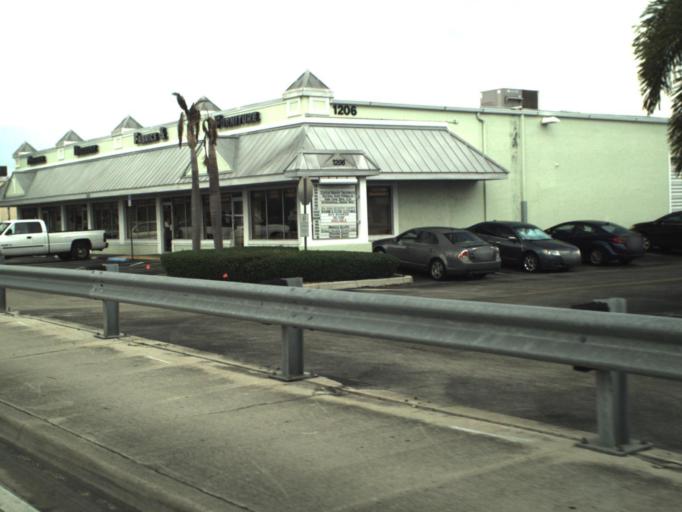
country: US
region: Florida
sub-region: Broward County
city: Dania Beach
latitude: 26.0485
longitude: -80.1522
